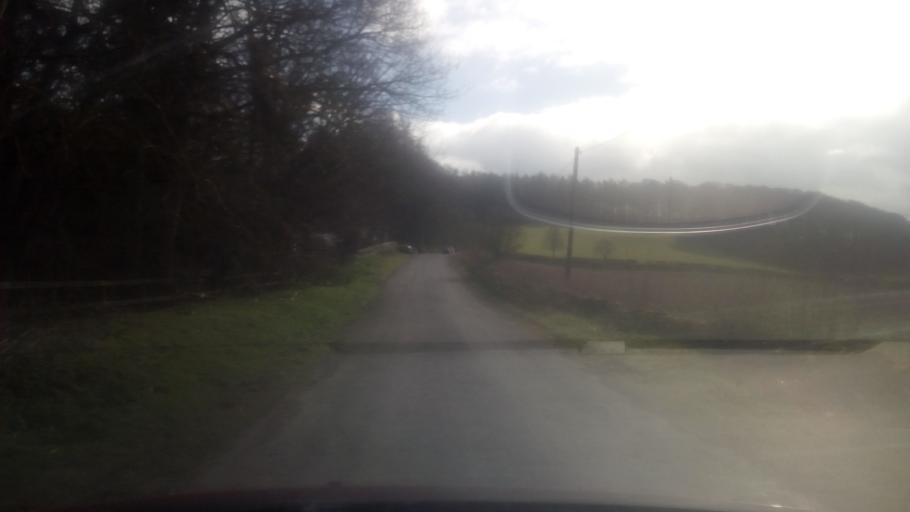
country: GB
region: Scotland
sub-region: The Scottish Borders
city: Jedburgh
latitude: 55.5056
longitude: -2.5736
